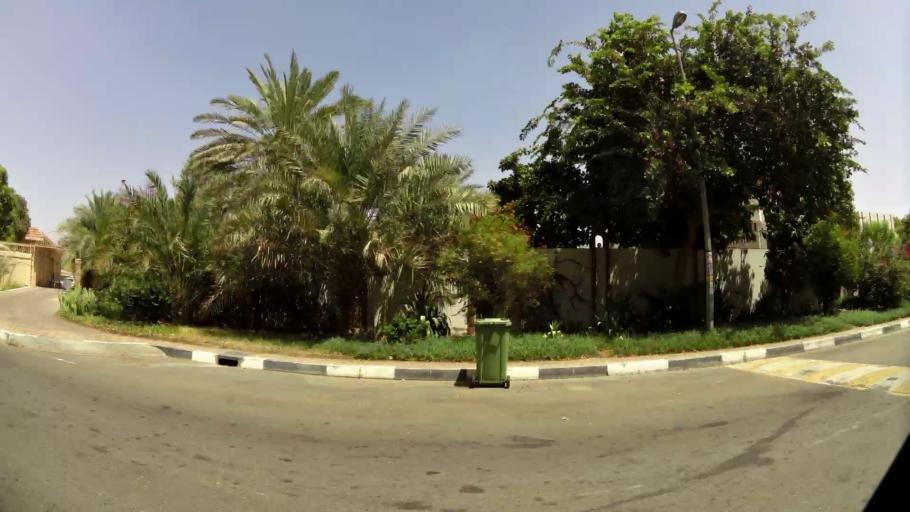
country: AE
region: Abu Dhabi
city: Al Ain
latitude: 24.2490
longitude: 55.6979
